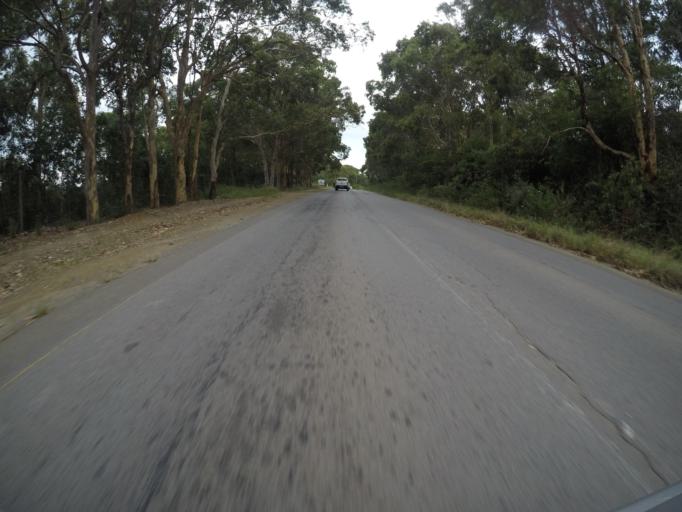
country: ZA
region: Eastern Cape
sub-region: Buffalo City Metropolitan Municipality
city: East London
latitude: -32.9372
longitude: 27.9437
